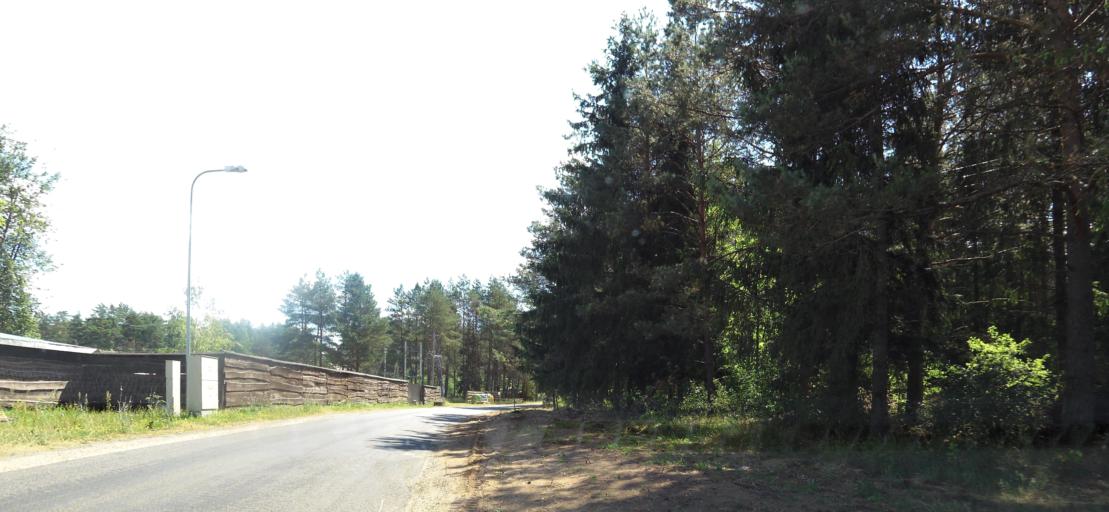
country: LT
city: Nemencine
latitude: 54.8214
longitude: 25.3982
